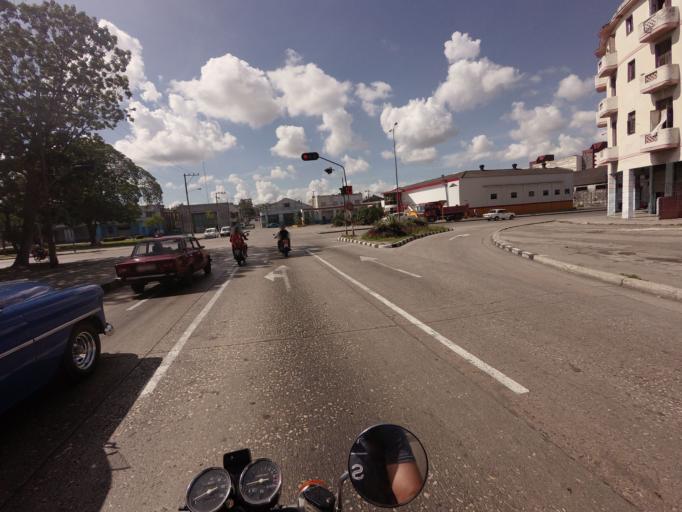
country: CU
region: La Habana
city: La Habana Vieja
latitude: 23.1141
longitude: -82.3593
